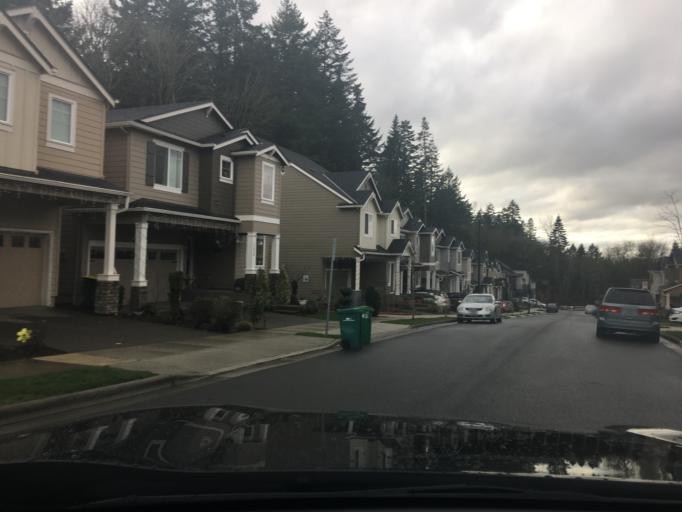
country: US
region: Oregon
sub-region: Washington County
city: Bethany
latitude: 45.5706
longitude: -122.8523
